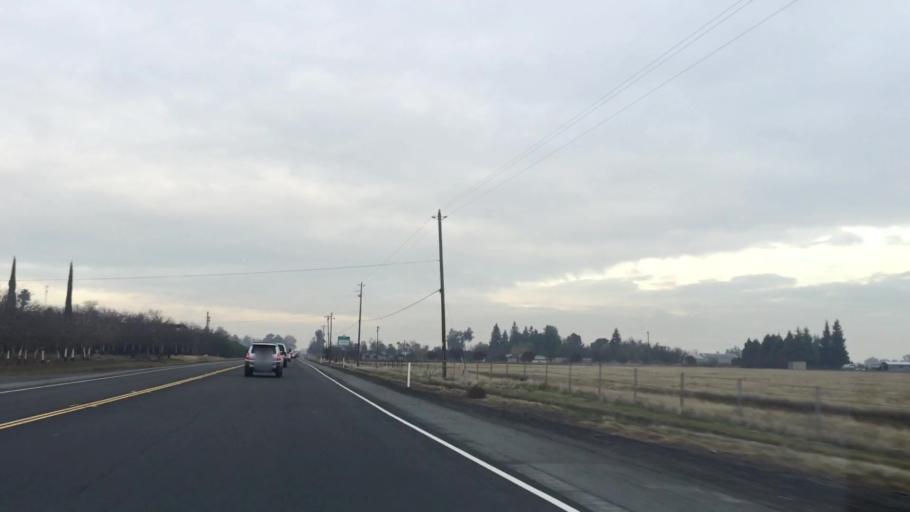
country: US
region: California
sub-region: Butte County
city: Palermo
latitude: 39.3950
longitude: -121.6048
